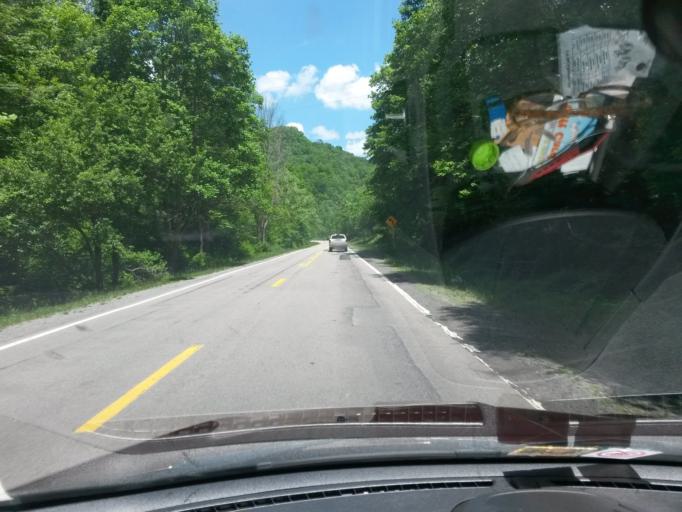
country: US
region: West Virginia
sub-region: Wyoming County
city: Mullens
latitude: 37.6532
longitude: -81.3860
